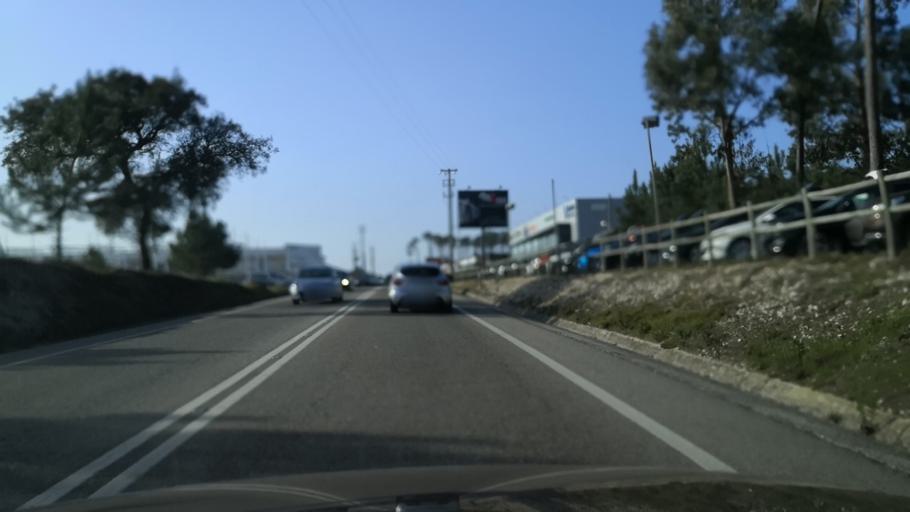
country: PT
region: Leiria
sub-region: Marinha Grande
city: Marinha Grande
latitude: 39.7457
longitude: -8.8961
